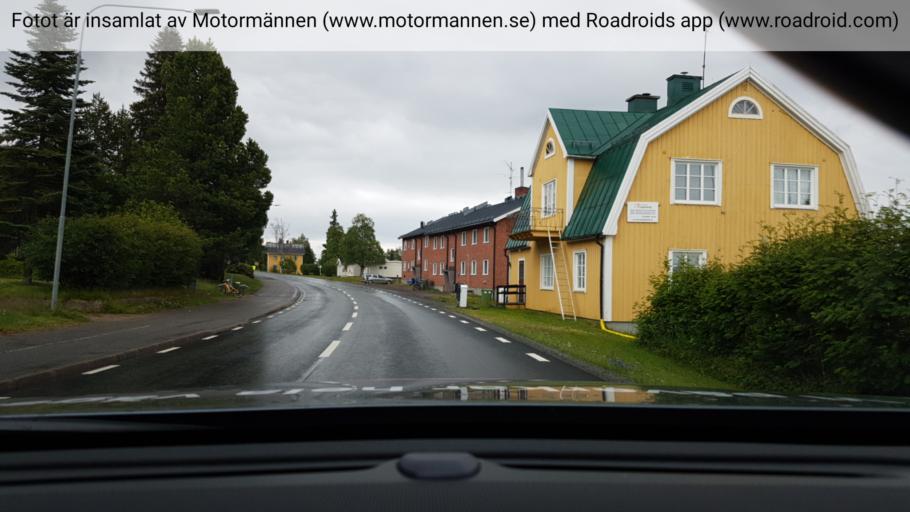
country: SE
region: Vaesterbotten
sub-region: Norsjo Kommun
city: Norsjoe
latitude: 65.2623
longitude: 19.6212
